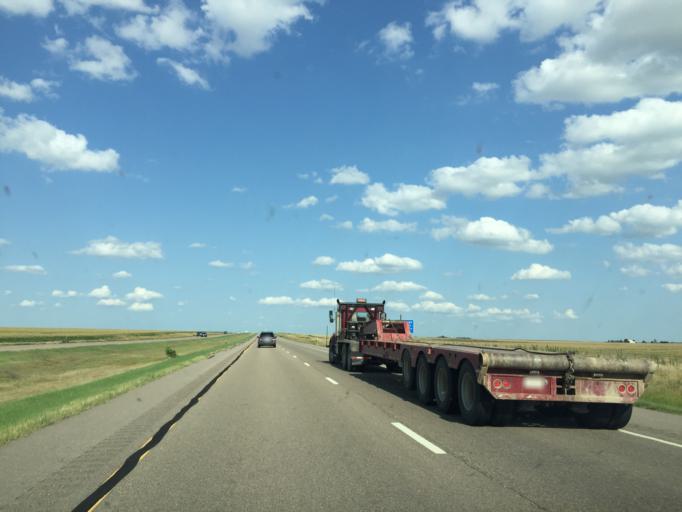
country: US
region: Kansas
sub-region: Trego County
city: WaKeeney
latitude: 39.0238
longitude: -100.1471
